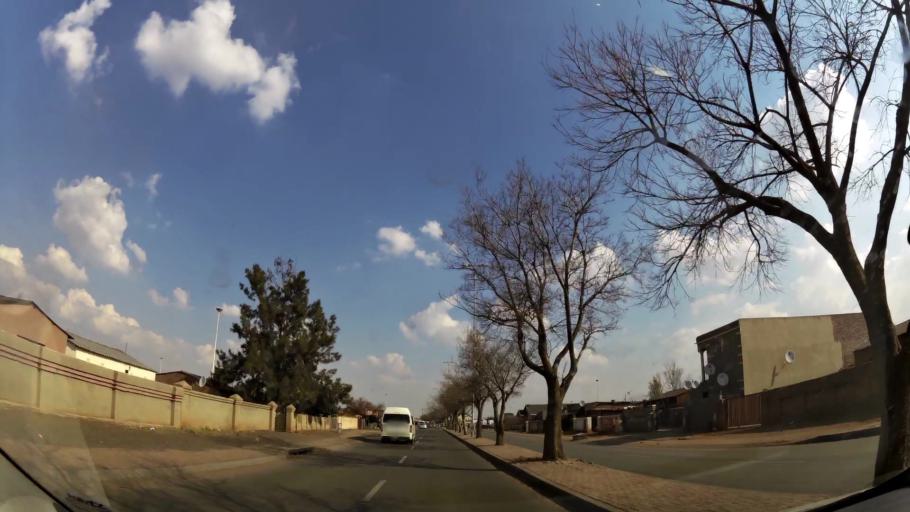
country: ZA
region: Gauteng
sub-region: Ekurhuleni Metropolitan Municipality
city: Germiston
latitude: -26.3254
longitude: 28.1538
